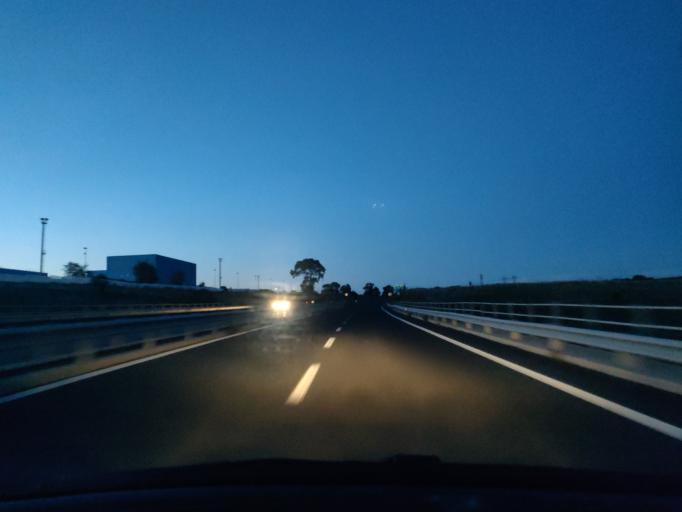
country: IT
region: Latium
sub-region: Citta metropolitana di Roma Capitale
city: Aurelia
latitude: 42.1221
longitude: 11.7910
